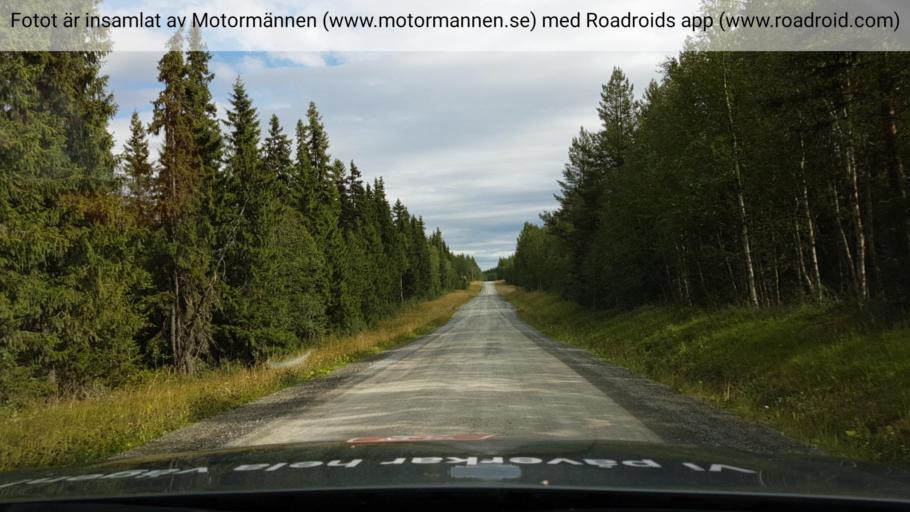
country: SE
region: Jaemtland
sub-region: Krokoms Kommun
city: Valla
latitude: 63.6482
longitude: 13.8125
